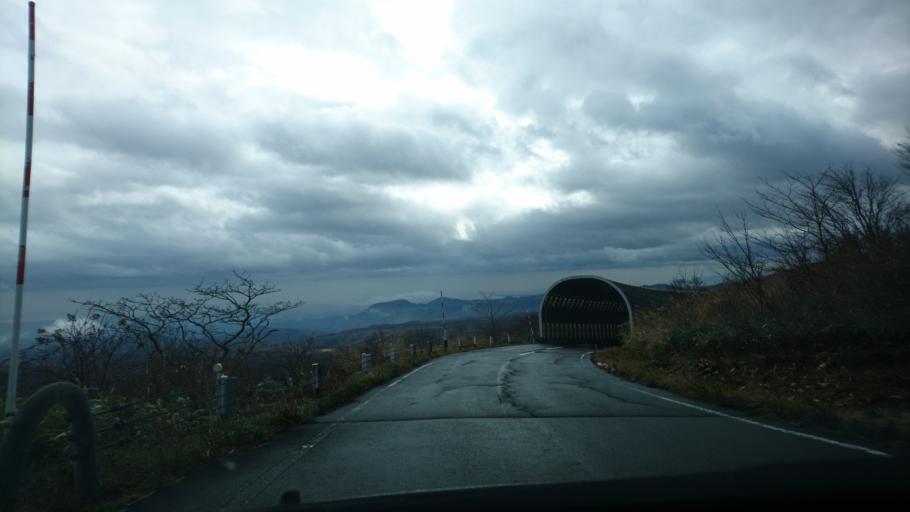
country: JP
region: Iwate
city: Ichinoseki
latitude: 38.9408
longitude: 140.8208
